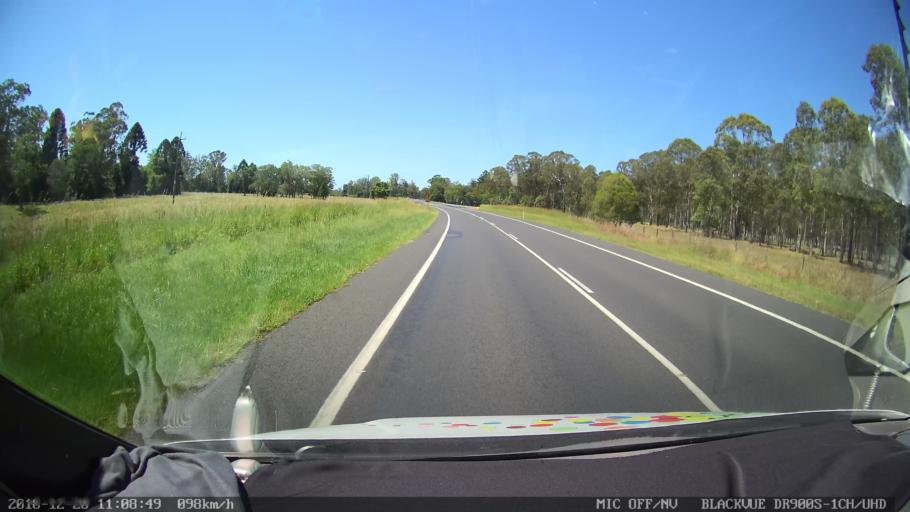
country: AU
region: New South Wales
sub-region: Richmond Valley
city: Casino
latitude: -28.9274
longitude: 153.0046
